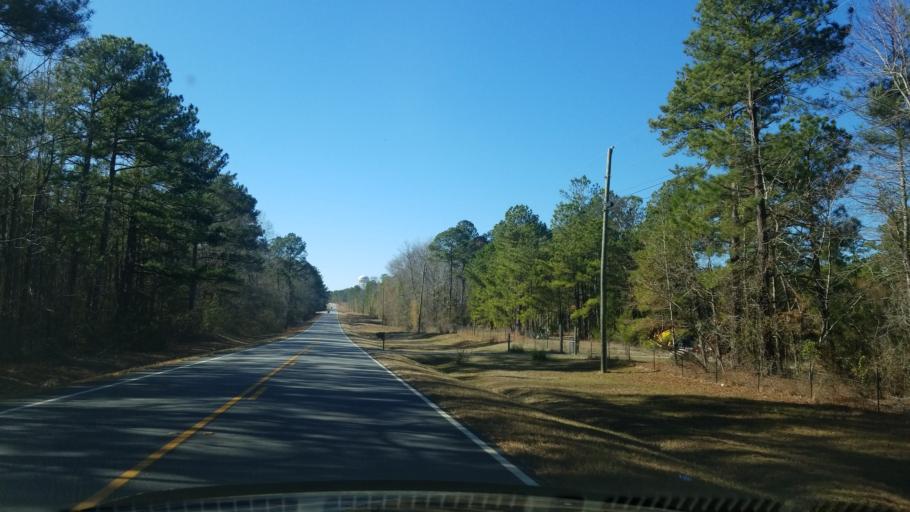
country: US
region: Georgia
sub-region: Harris County
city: Hamilton
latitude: 32.6320
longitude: -84.7506
